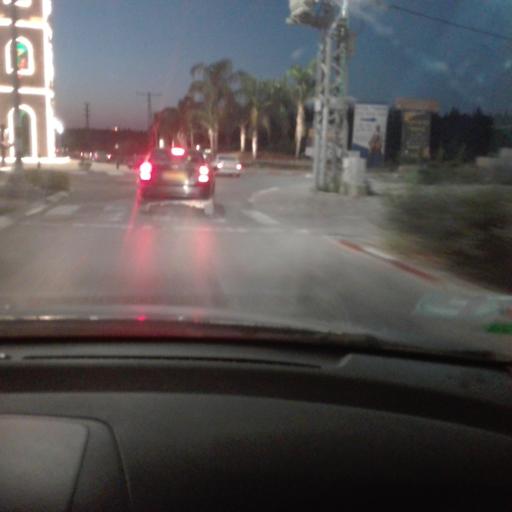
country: PS
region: West Bank
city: Nazlat `Isa
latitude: 32.4292
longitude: 35.0308
